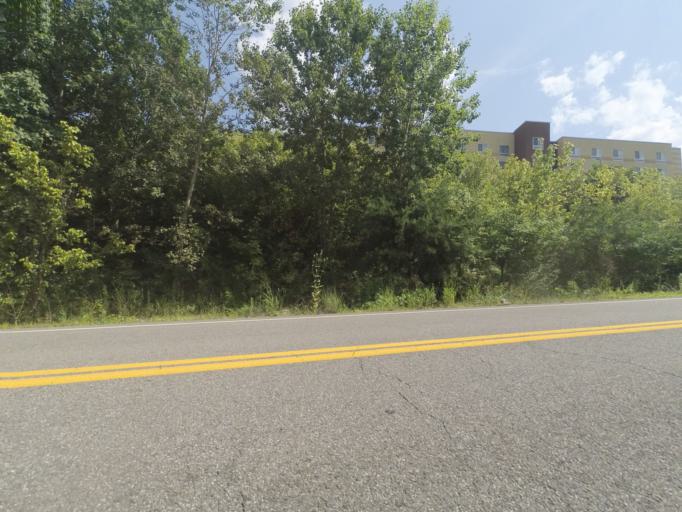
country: US
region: West Virginia
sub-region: Cabell County
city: Huntington
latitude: 38.3960
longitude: -82.4226
